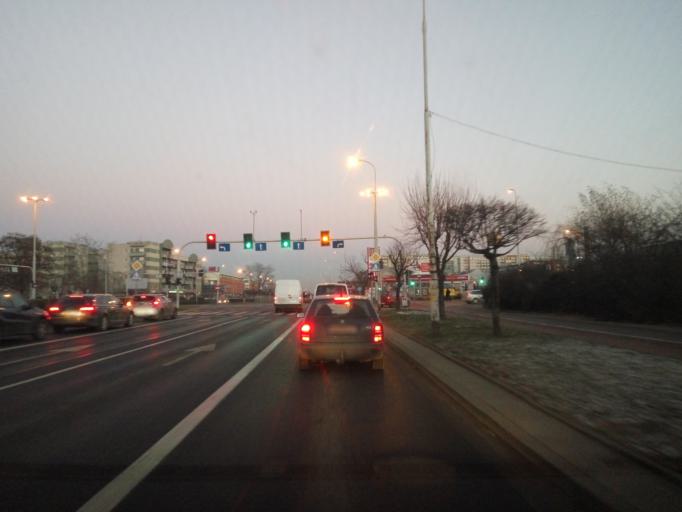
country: PL
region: Lower Silesian Voivodeship
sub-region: Powiat wroclawski
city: Wroclaw
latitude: 51.0831
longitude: 17.0337
